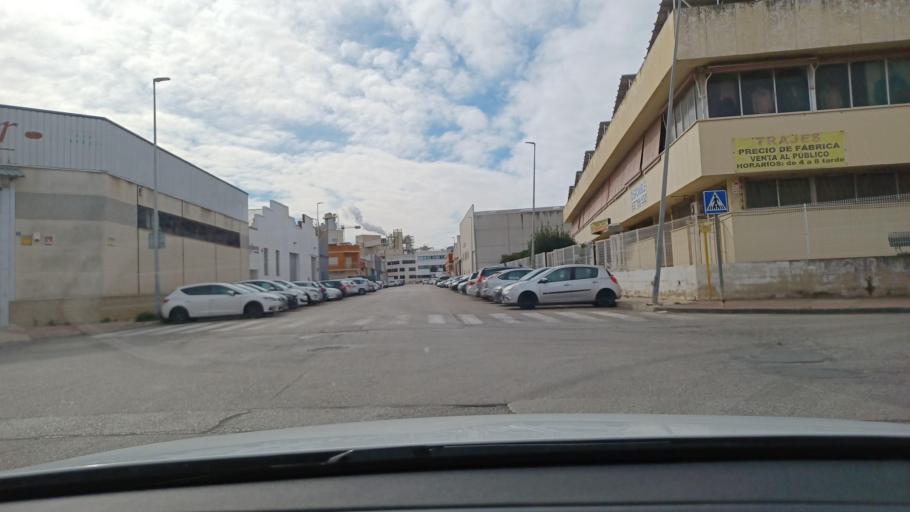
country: ES
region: Valencia
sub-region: Provincia de Valencia
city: Benifaio
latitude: 39.2866
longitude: -0.4322
